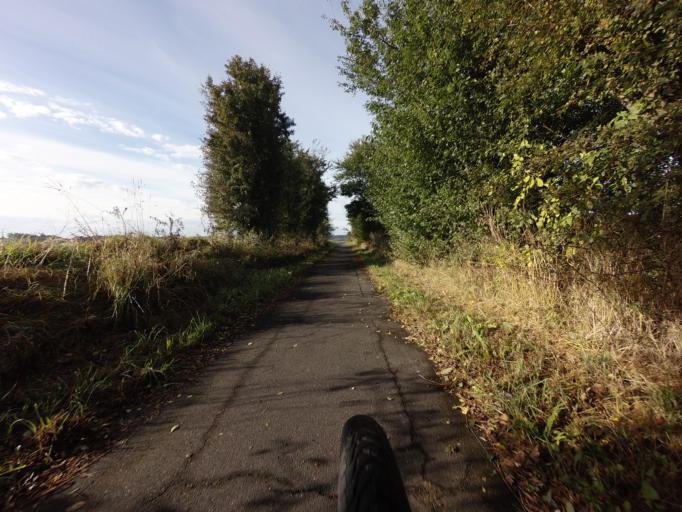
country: DK
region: Central Jutland
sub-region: Viborg Kommune
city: Bjerringbro
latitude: 56.4460
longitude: 9.5734
